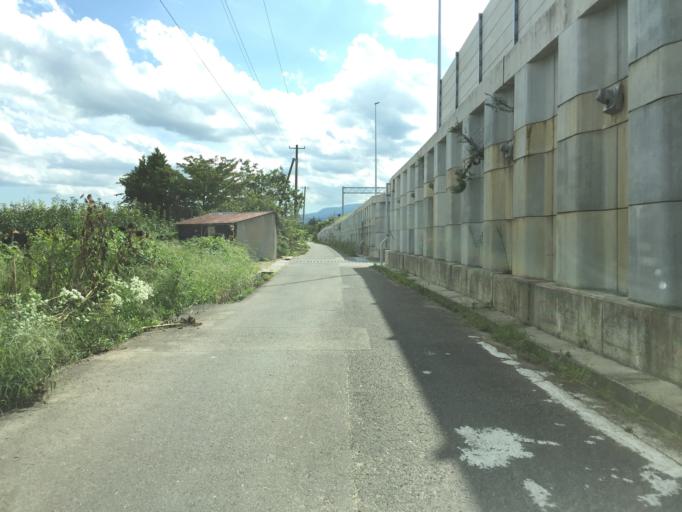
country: JP
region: Fukushima
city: Fukushima-shi
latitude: 37.7861
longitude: 140.4158
